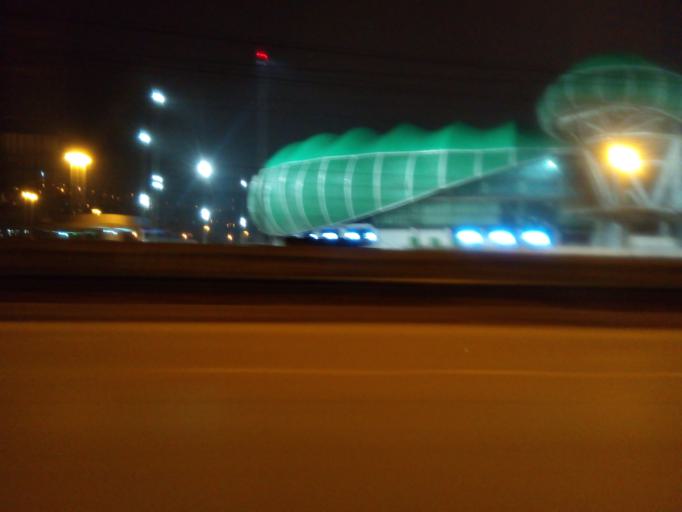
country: TR
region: Bursa
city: Yildirim
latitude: 40.2124
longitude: 29.0100
